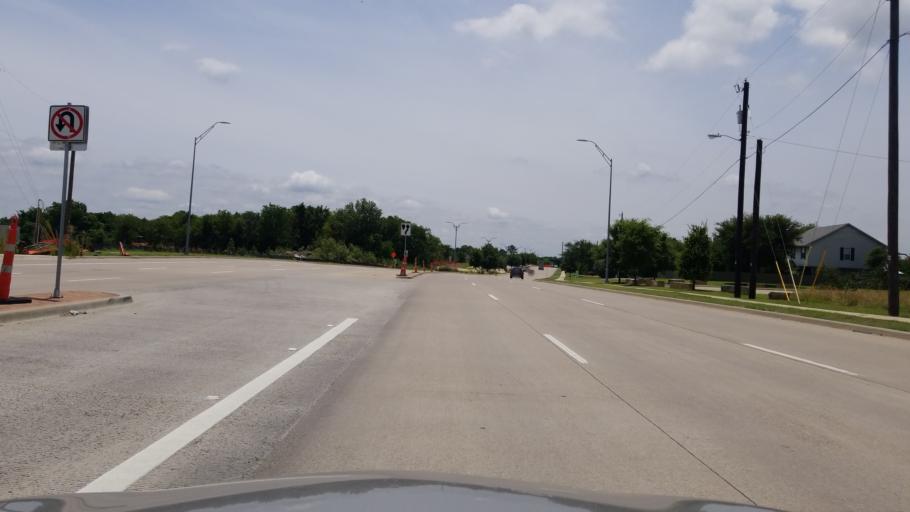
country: US
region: Texas
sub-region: Dallas County
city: Grand Prairie
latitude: 32.6743
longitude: -97.0238
